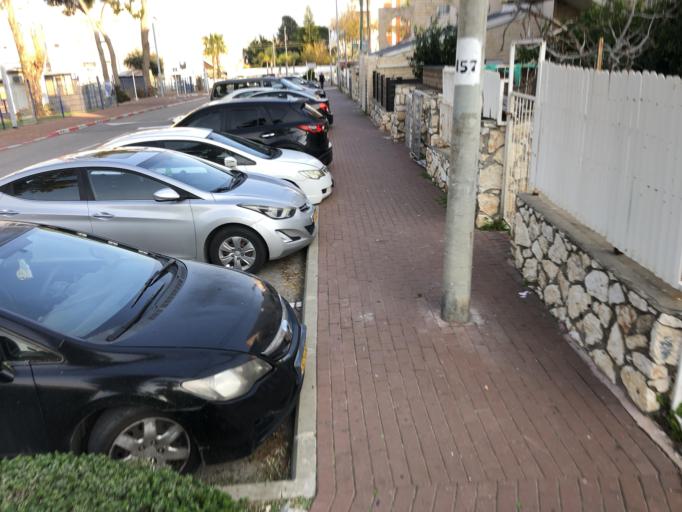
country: IL
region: Northern District
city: `Akko
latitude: 32.9259
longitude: 35.0908
